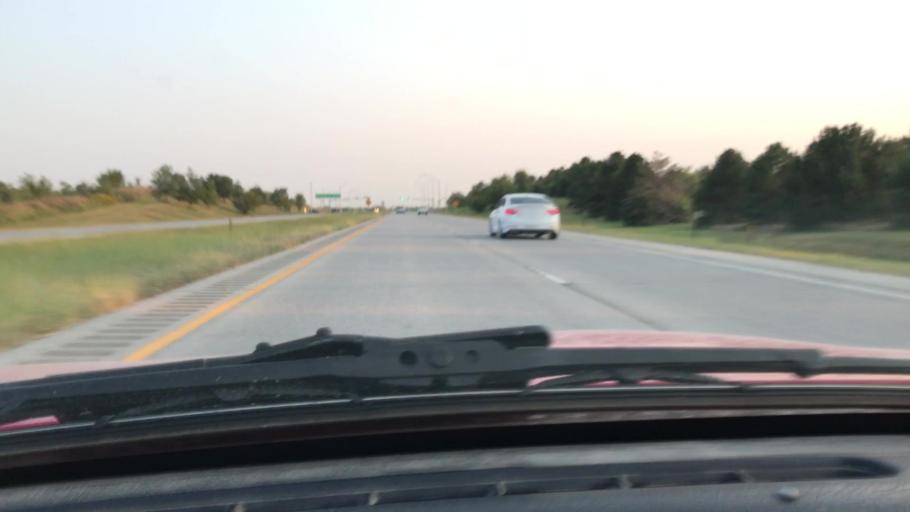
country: US
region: Nebraska
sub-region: Lancaster County
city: Lincoln
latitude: 40.7739
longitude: -96.7274
